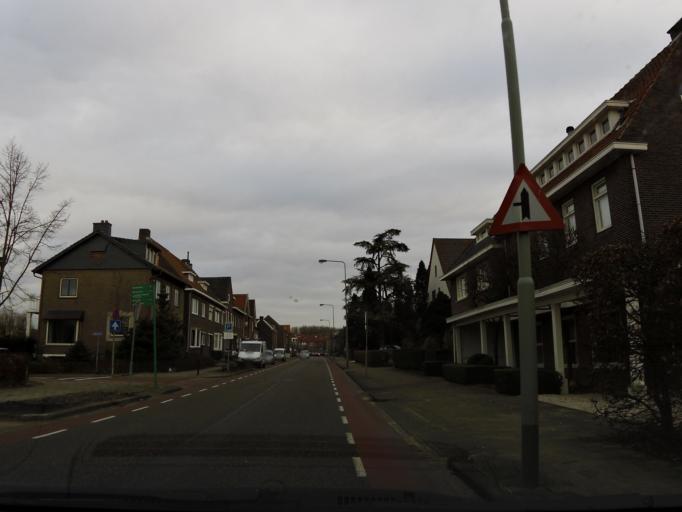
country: NL
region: Limburg
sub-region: Gemeente Schinnen
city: Schinnen
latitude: 50.9409
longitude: 5.8845
